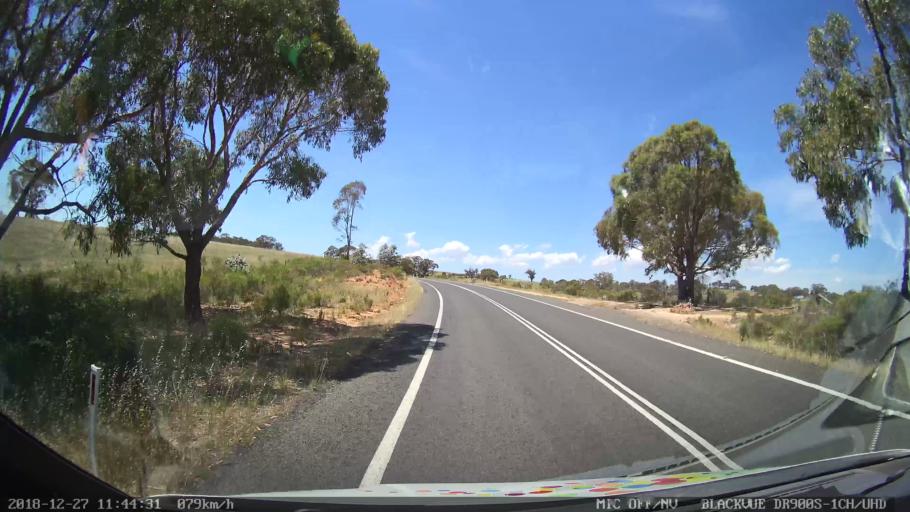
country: AU
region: New South Wales
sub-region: Bathurst Regional
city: Perthville
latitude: -33.5730
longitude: 149.4753
